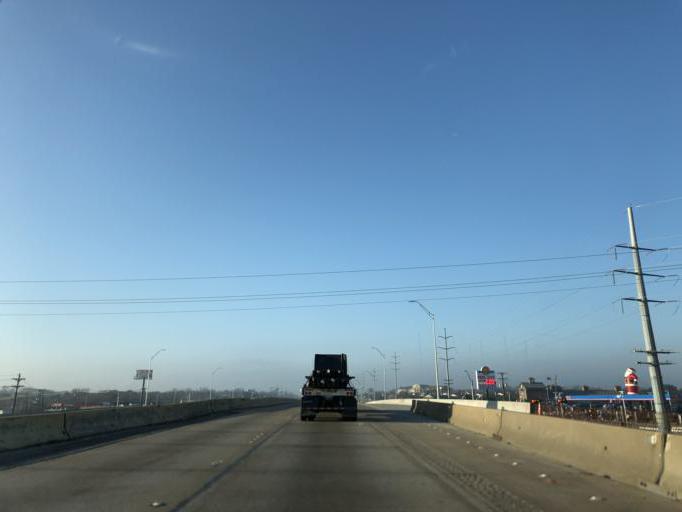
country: US
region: Texas
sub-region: Dallas County
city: Cedar Hill
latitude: 32.6109
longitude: -96.9249
